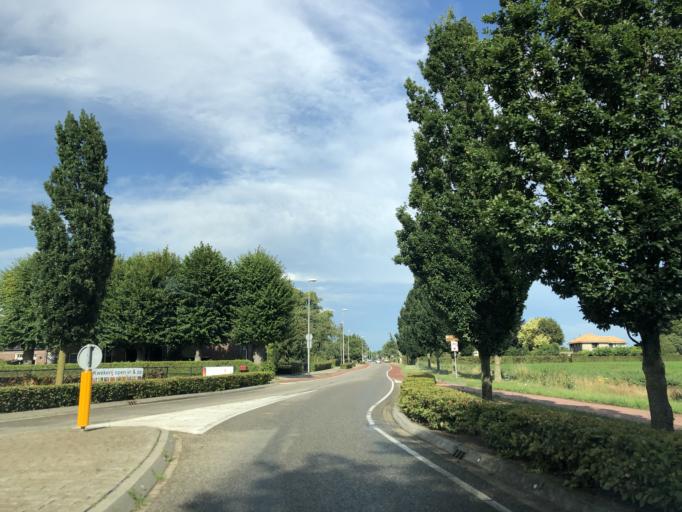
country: NL
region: Limburg
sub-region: Gemeente Gennep
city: Gennep
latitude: 51.7089
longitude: 6.0123
